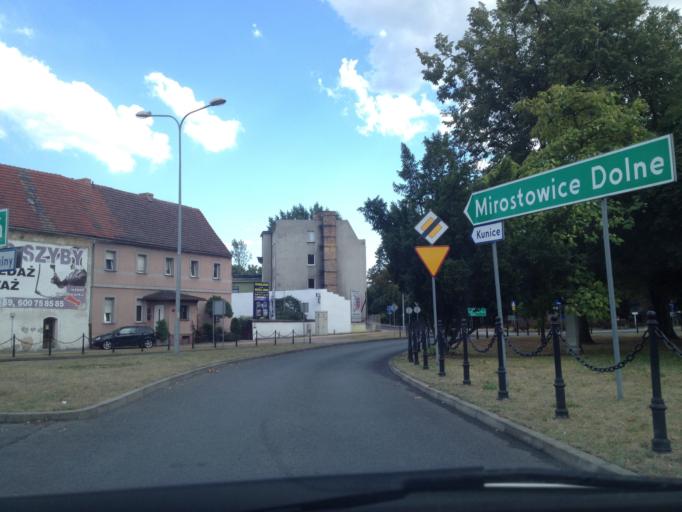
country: PL
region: Lubusz
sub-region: Powiat zarski
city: Zary
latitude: 51.6391
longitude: 15.1477
